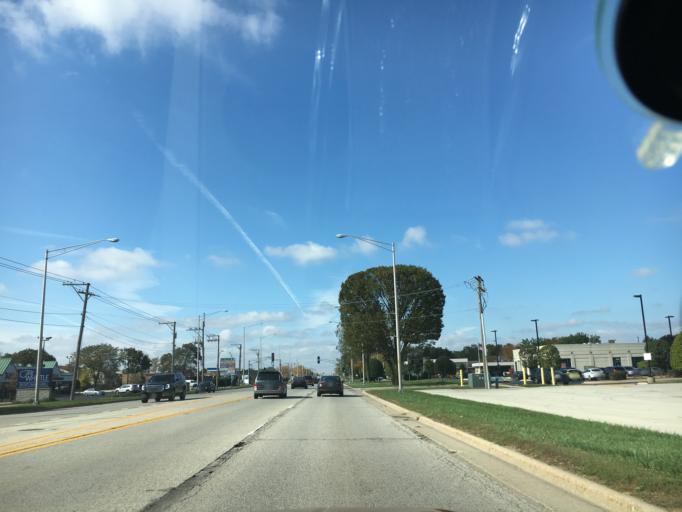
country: US
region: Illinois
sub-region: Cook County
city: Tinley Park
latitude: 41.6022
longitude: -87.8019
